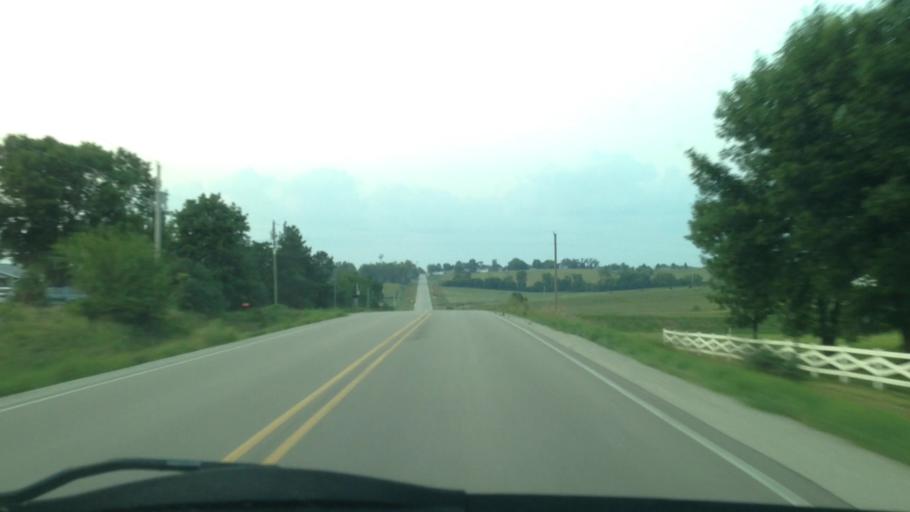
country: US
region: Iowa
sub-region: Benton County
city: Urbana
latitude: 42.2108
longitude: -91.8715
